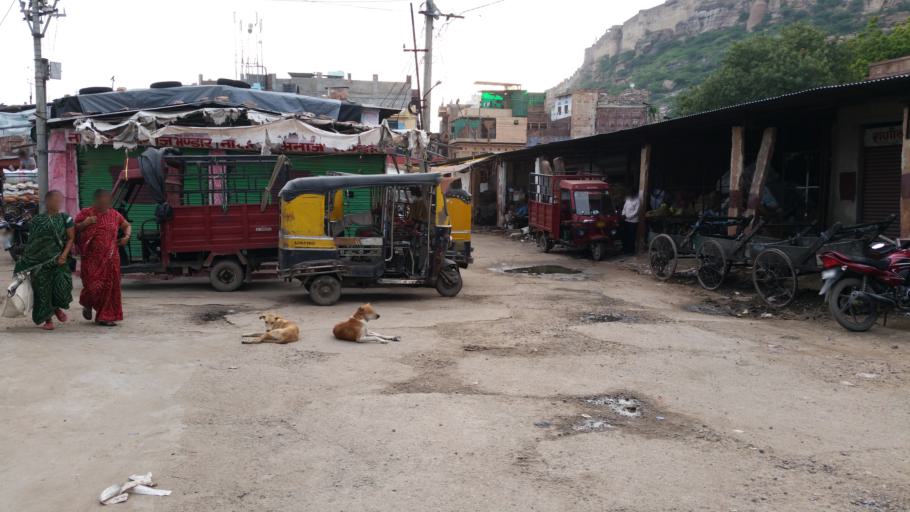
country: IN
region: Rajasthan
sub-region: Jodhpur
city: Jodhpur
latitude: 26.2946
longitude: 73.0225
